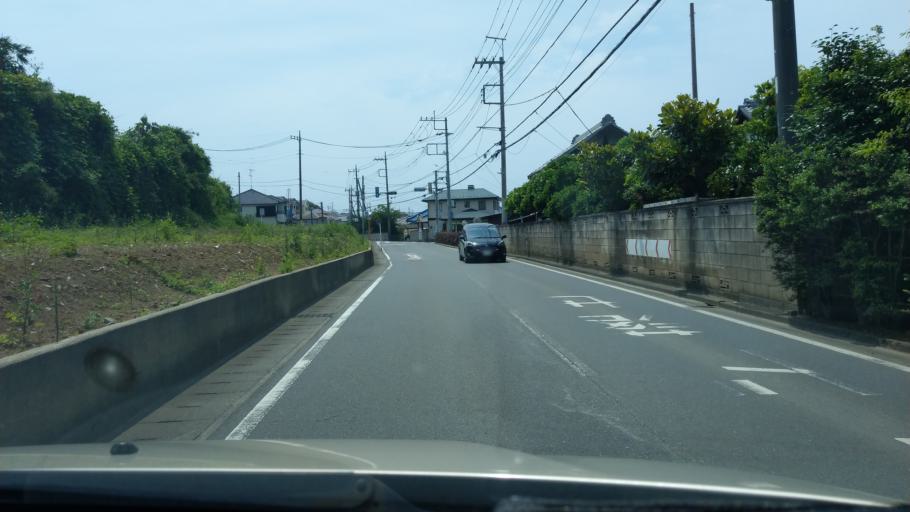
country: JP
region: Saitama
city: Saitama
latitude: 35.9044
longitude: 139.6502
